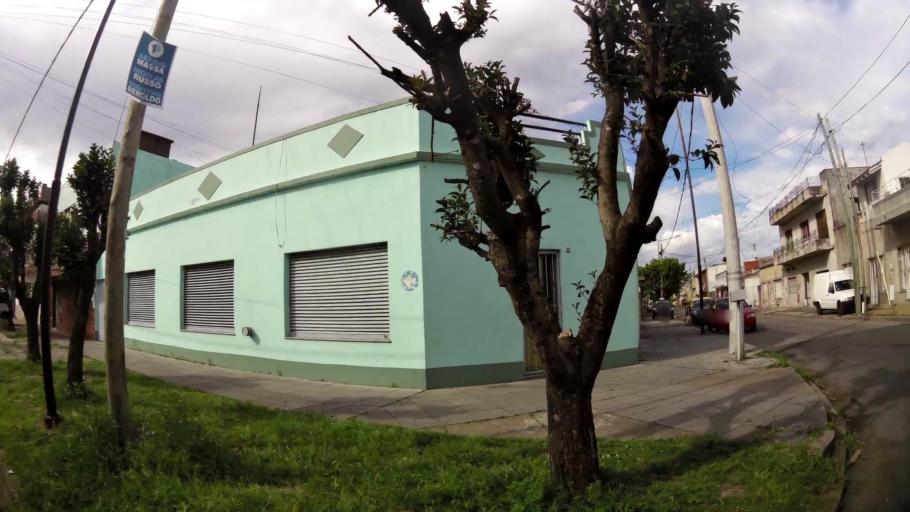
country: AR
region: Buenos Aires
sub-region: Partido de Lanus
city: Lanus
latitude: -34.6938
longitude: -58.3808
